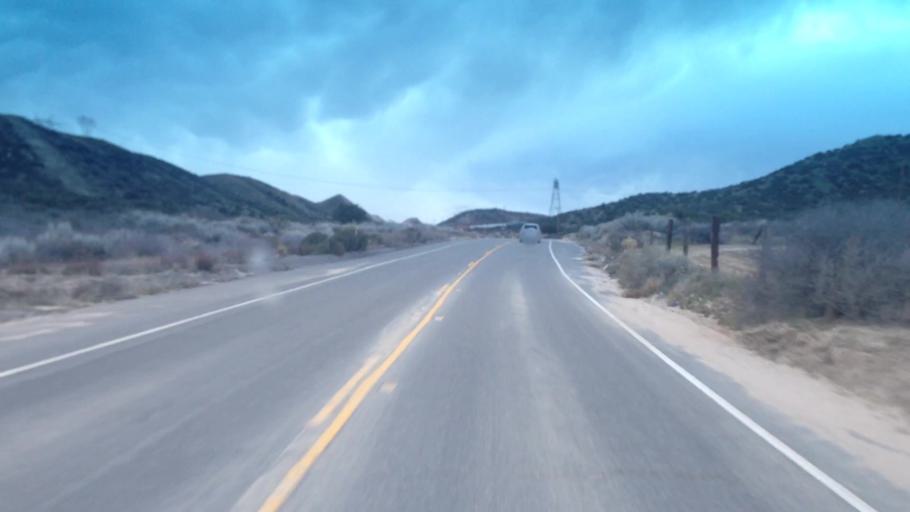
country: US
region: California
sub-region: San Bernardino County
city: Oak Hills
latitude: 34.3246
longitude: -117.4112
